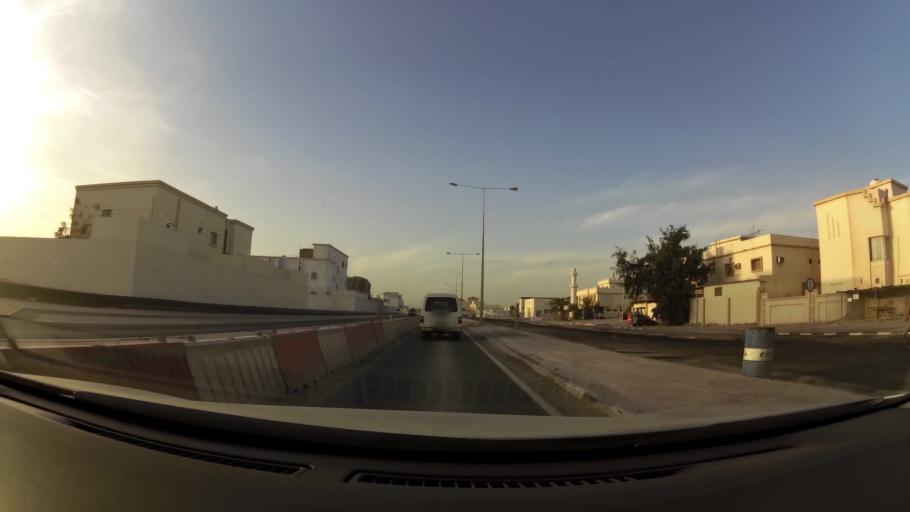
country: QA
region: Al Wakrah
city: Al Wakrah
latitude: 25.1561
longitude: 51.5925
